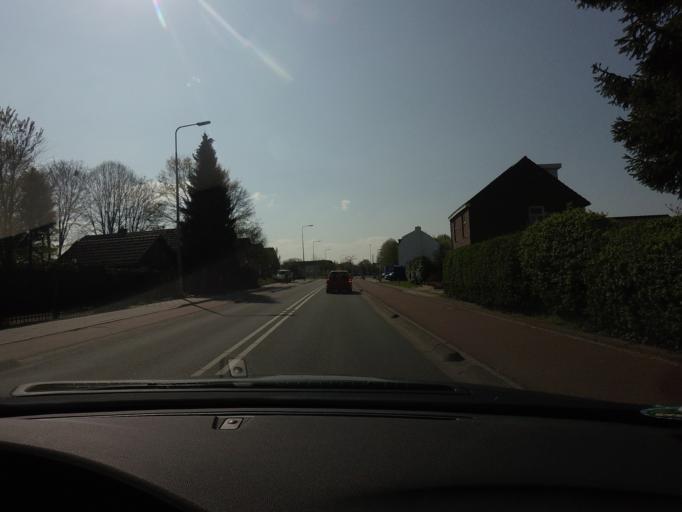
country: NL
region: Limburg
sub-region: Gemeente Maastricht
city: Heer
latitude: 50.8287
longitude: 5.7291
